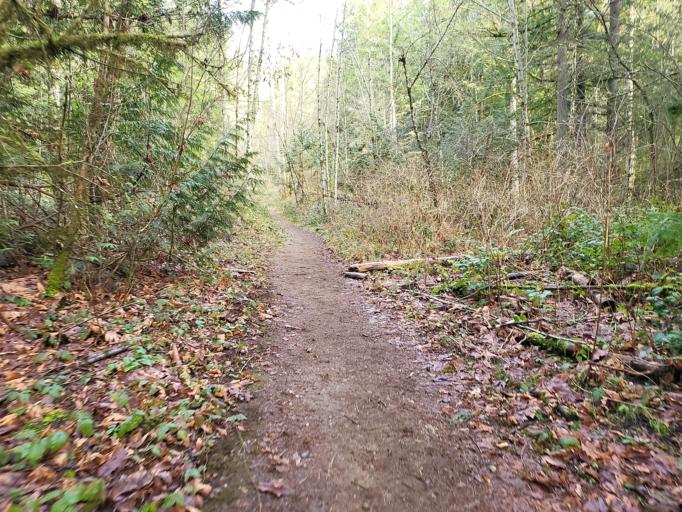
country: US
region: Washington
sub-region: King County
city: Issaquah
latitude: 47.5242
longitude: -122.0254
